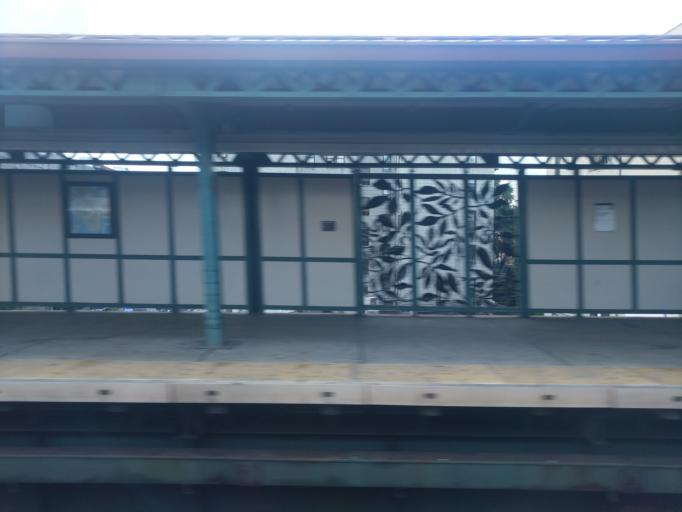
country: US
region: New York
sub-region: Bronx
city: The Bronx
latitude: 40.8288
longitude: -73.8790
